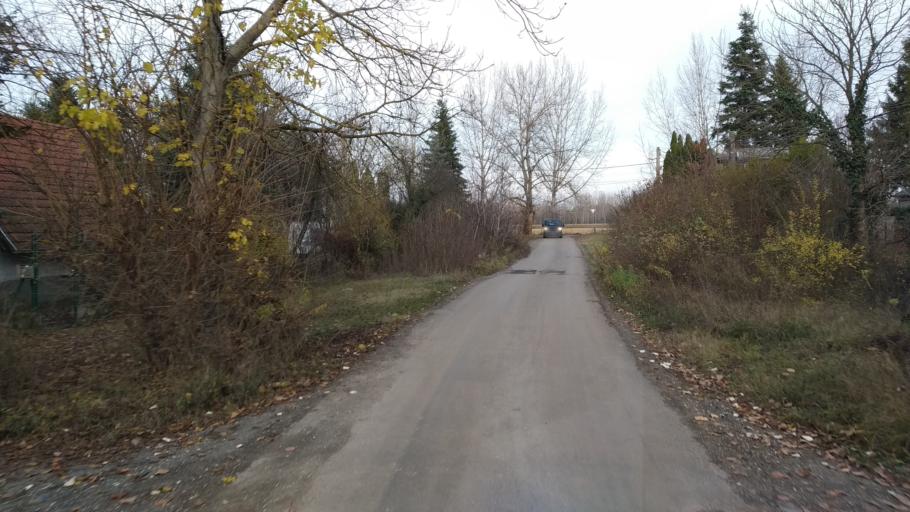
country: HU
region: Pest
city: God
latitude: 47.6846
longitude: 19.1142
